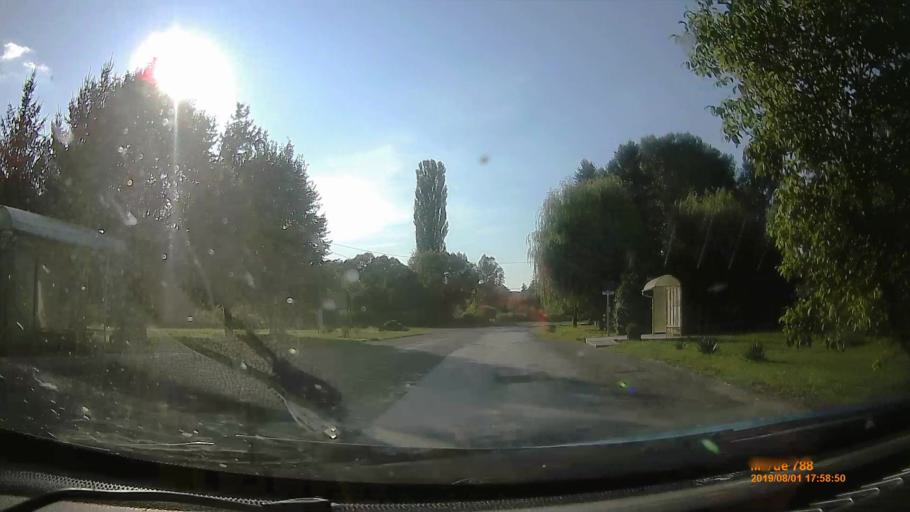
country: HU
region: Baranya
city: Sasd
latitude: 46.2032
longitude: 18.1105
